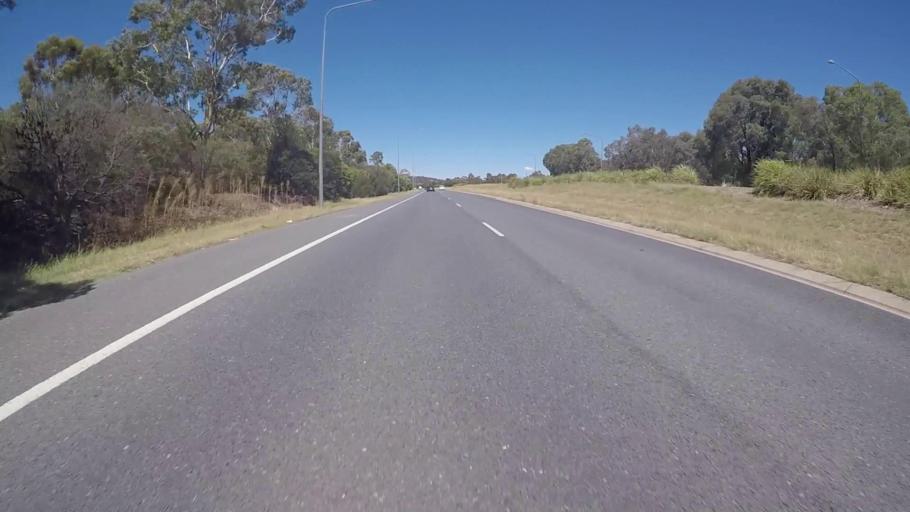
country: AU
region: Australian Capital Territory
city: Macarthur
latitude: -35.4182
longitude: 149.0758
